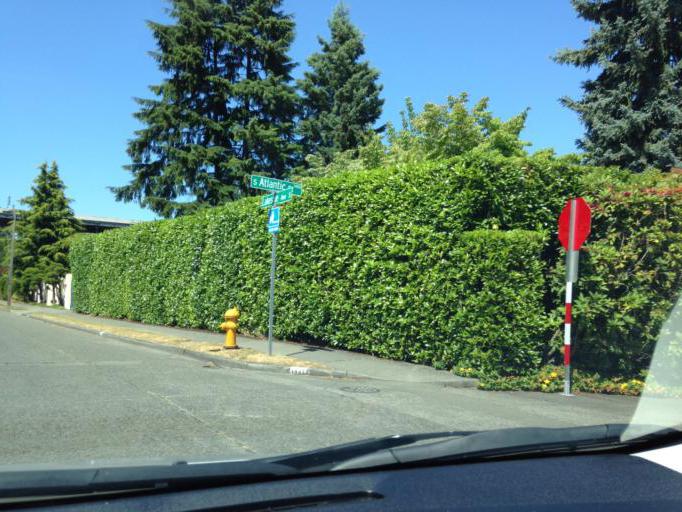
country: US
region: Washington
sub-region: King County
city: Seattle
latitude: 47.5888
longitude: -122.2861
